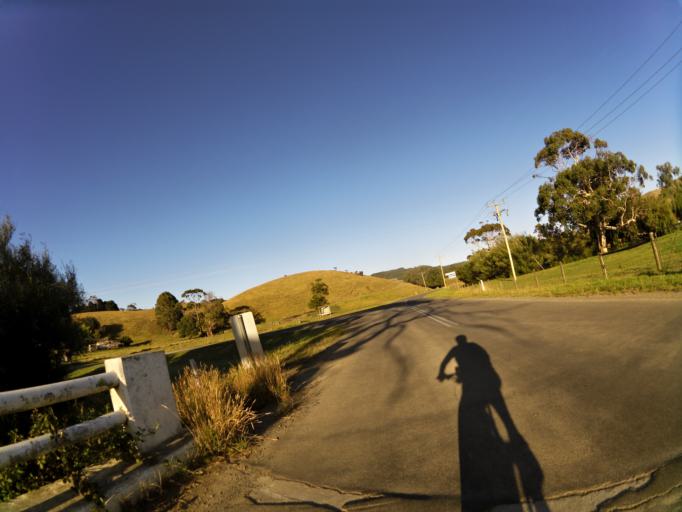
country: AU
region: Victoria
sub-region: Colac-Otway
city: Apollo Bay
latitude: -38.7695
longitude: 143.6473
